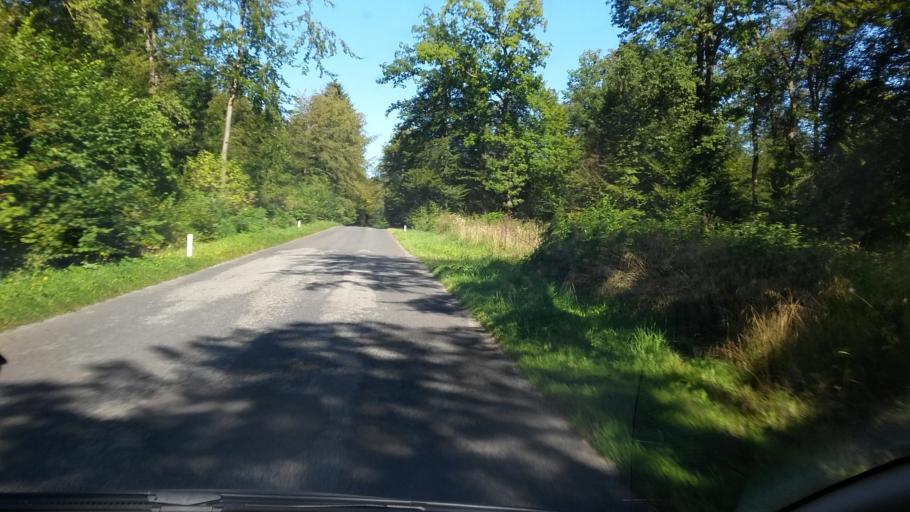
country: BE
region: Wallonia
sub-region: Province du Luxembourg
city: Neufchateau
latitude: 49.8023
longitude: 5.4154
